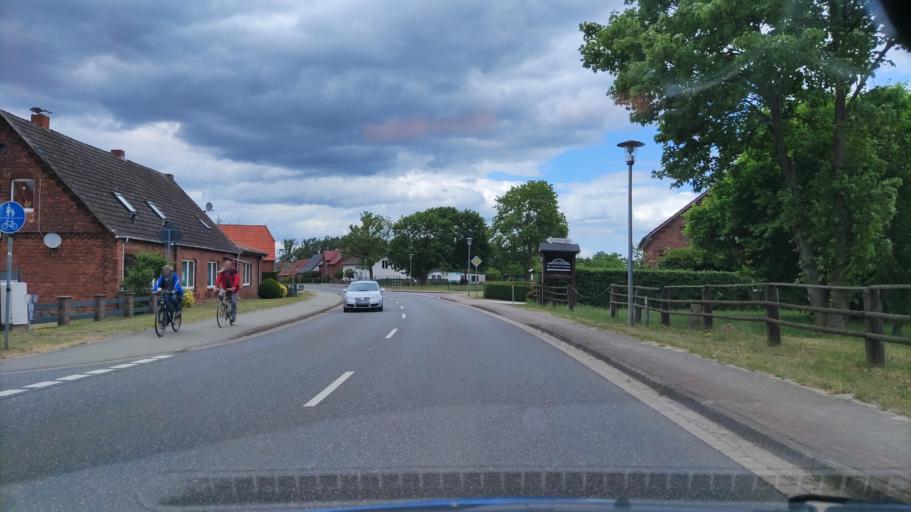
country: DE
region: Mecklenburg-Vorpommern
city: Spornitz
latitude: 53.4079
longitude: 11.7231
